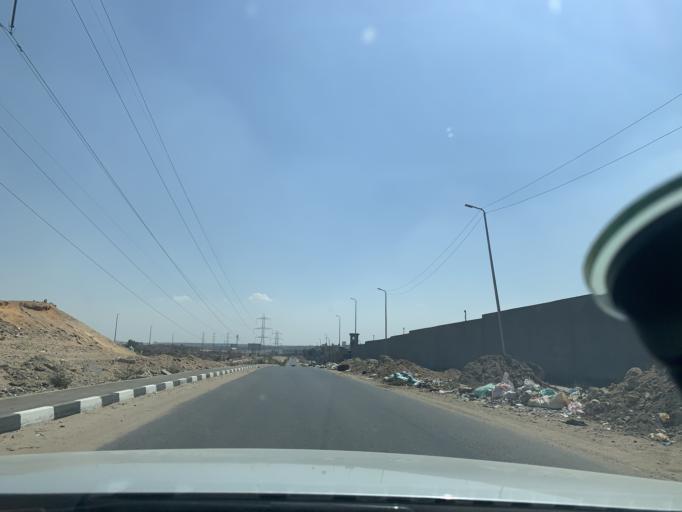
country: EG
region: Muhafazat al Qahirah
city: Cairo
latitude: 30.0329
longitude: 31.3518
